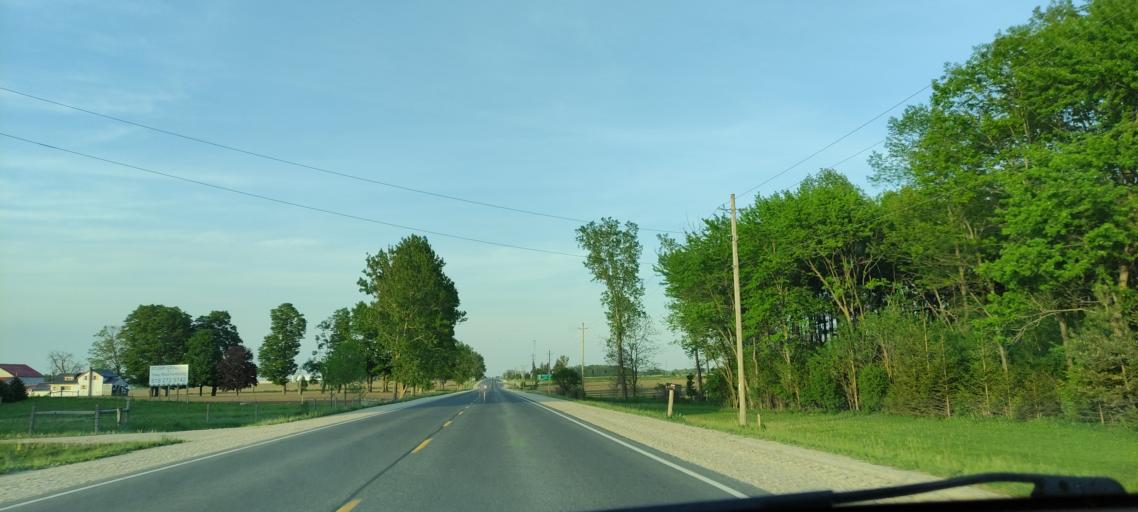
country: CA
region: Ontario
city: London
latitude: 43.2199
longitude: -81.1695
